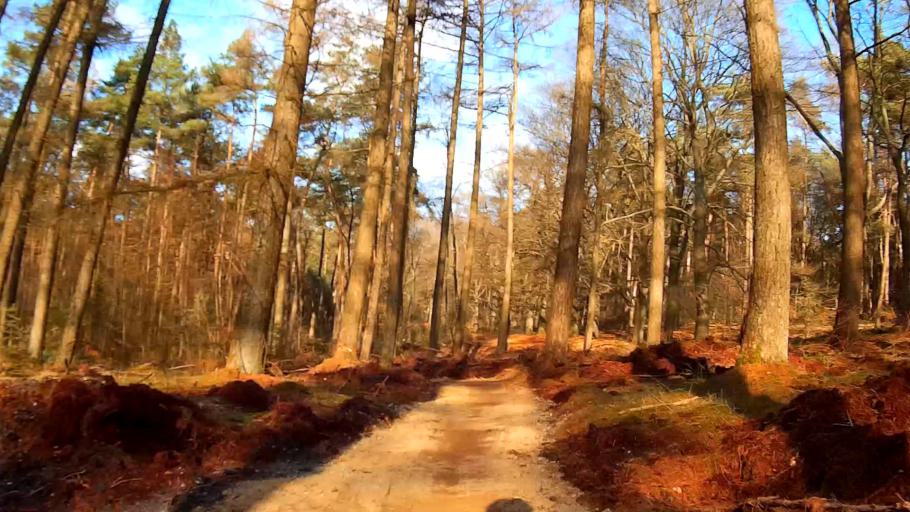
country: NL
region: Utrecht
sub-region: Gemeente Utrechtse Heuvelrug
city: Amerongen
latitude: 52.0182
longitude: 5.4692
